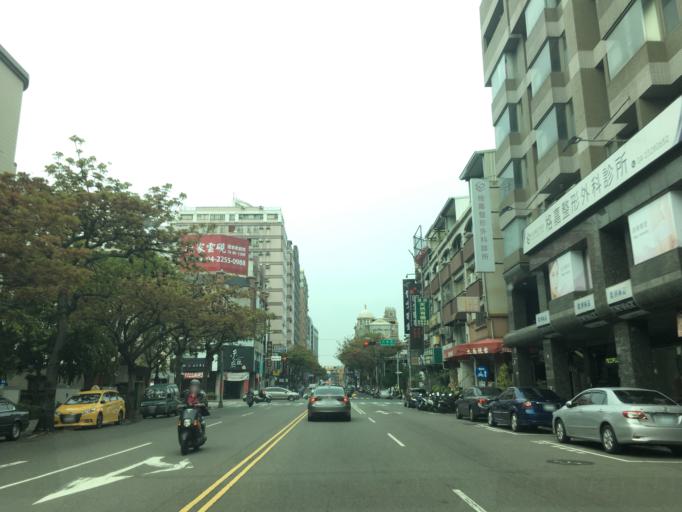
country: TW
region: Taiwan
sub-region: Taichung City
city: Taichung
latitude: 24.1552
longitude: 120.6535
